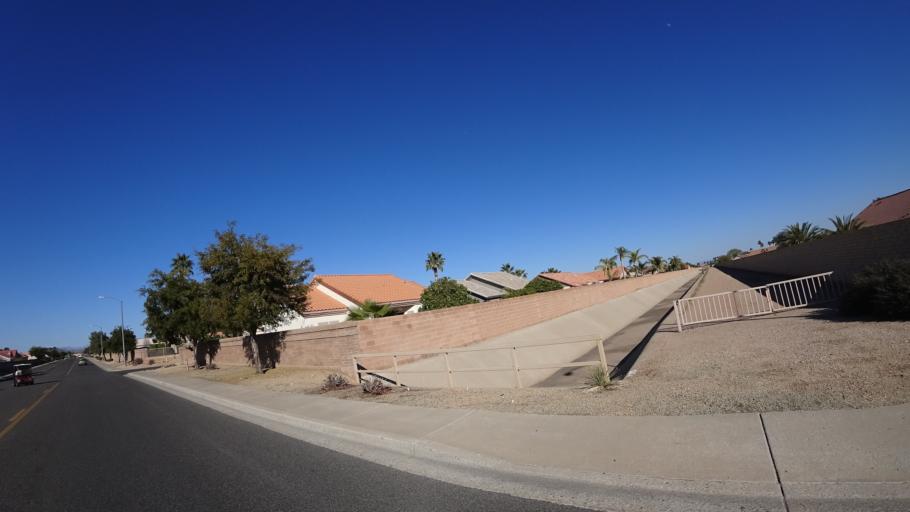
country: US
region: Arizona
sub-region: Maricopa County
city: Sun City West
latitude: 33.6819
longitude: -112.3815
